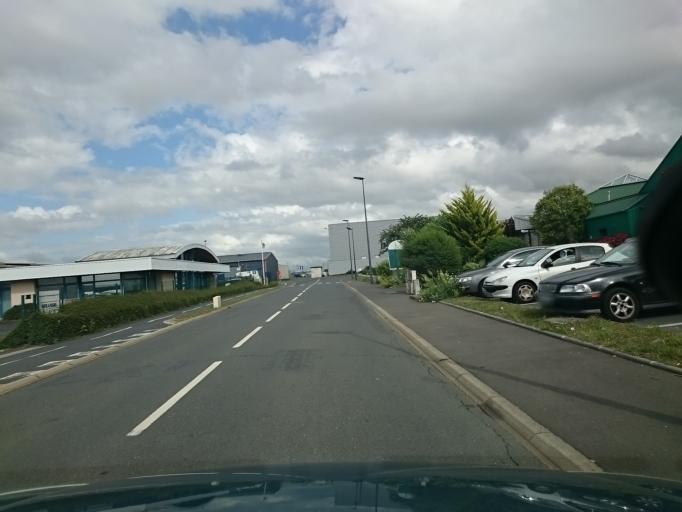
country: FR
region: Lower Normandy
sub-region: Departement du Calvados
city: Ifs
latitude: 49.1424
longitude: -0.3418
